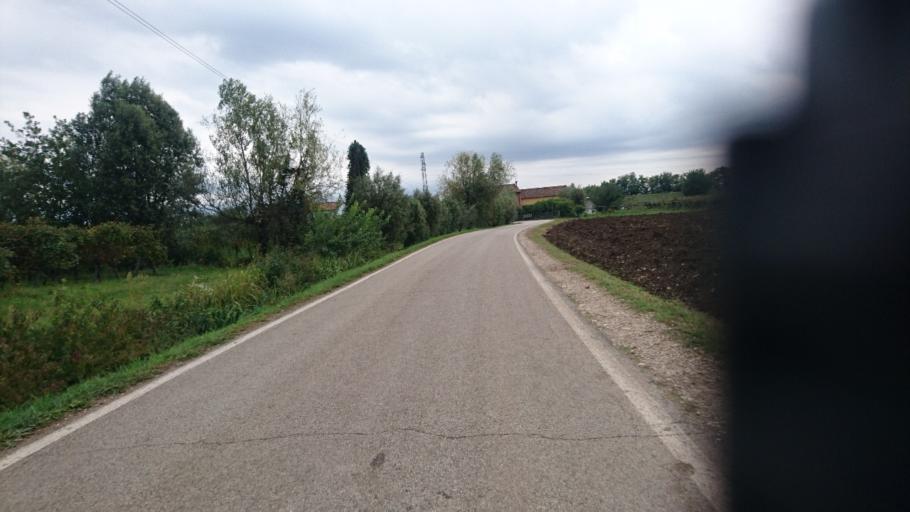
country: IT
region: Veneto
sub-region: Provincia di Vicenza
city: Gambellara
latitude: 45.4358
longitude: 11.3429
